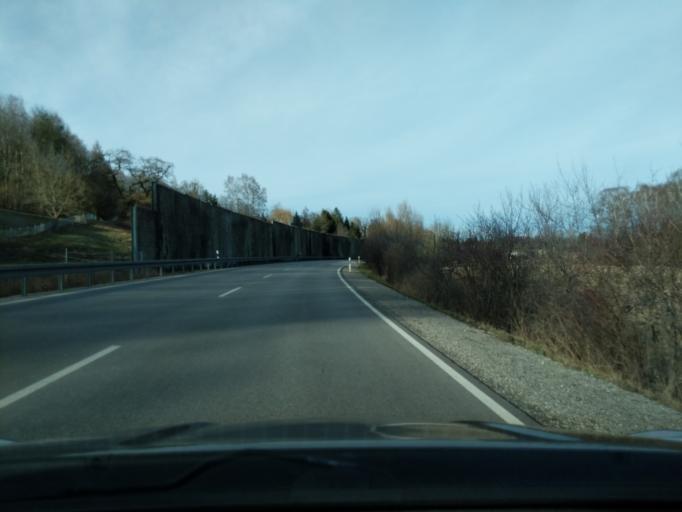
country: DE
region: Bavaria
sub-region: Upper Bavaria
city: Ebersberg
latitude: 48.0698
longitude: 11.9773
